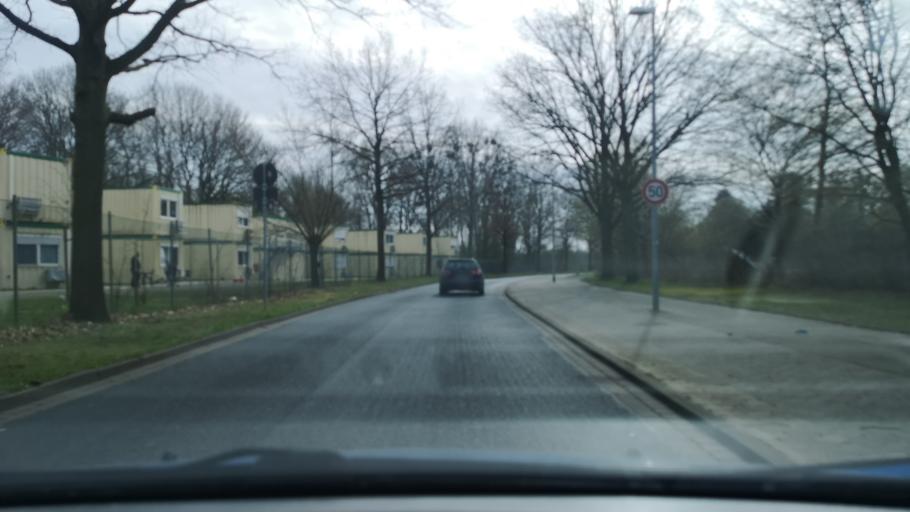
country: DE
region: Lower Saxony
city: Hannover
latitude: 52.4079
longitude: 9.6744
